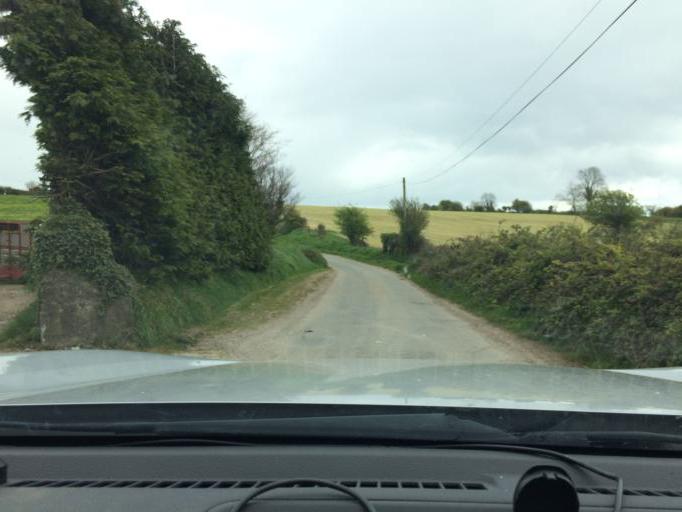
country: IE
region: Munster
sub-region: Waterford
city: Dungarvan
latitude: 52.0546
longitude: -7.6122
